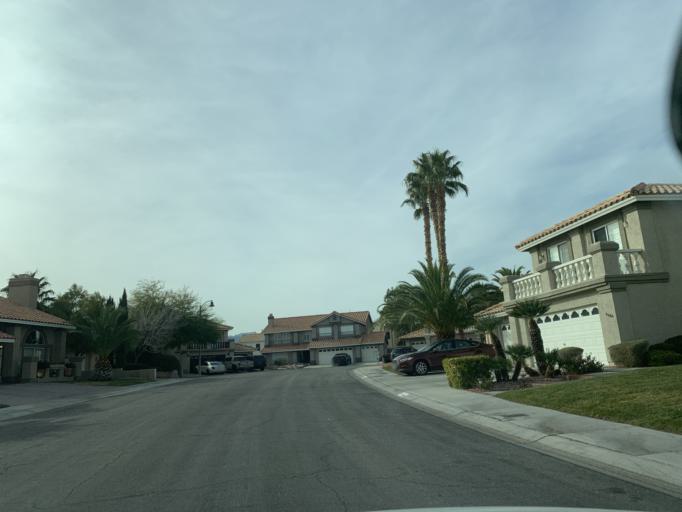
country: US
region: Nevada
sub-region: Clark County
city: Summerlin South
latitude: 36.1358
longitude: -115.3008
